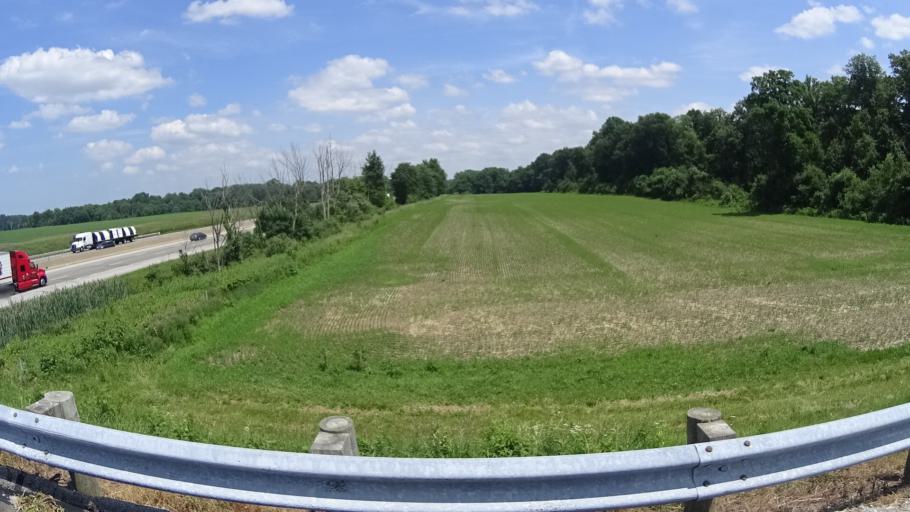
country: US
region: Ohio
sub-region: Erie County
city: Huron
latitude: 41.3250
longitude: -82.5357
